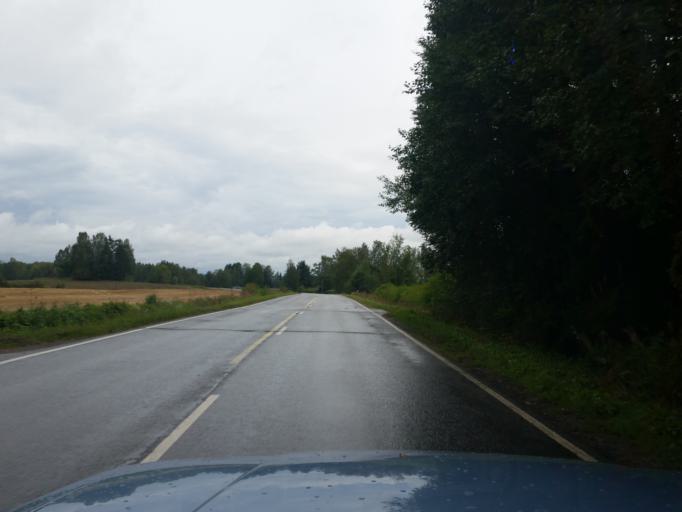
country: FI
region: Uusimaa
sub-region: Helsinki
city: Saukkola
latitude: 60.4865
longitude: 23.9674
